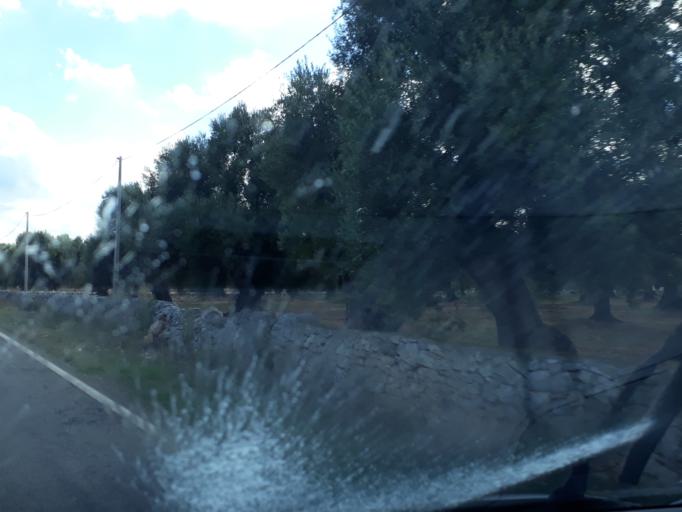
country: IT
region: Apulia
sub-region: Provincia di Brindisi
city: Fasano
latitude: 40.8219
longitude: 17.3748
